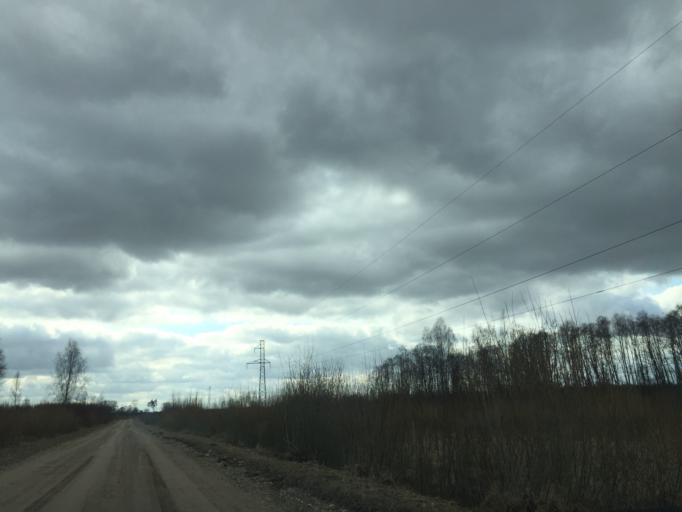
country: LV
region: Vecumnieki
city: Vecumnieki
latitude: 56.5743
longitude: 24.6014
